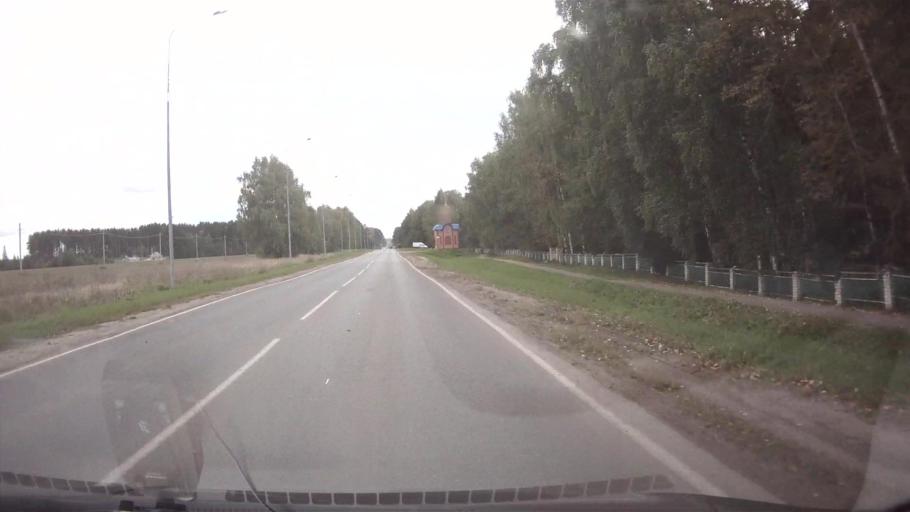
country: RU
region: Mariy-El
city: Kuzhener
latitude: 56.9947
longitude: 48.7426
